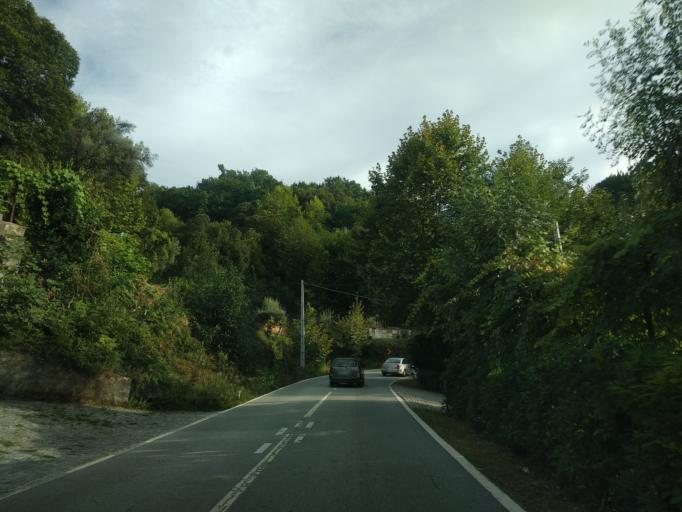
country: PT
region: Braga
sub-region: Vieira do Minho
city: Real
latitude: 41.6612
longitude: -8.1745
